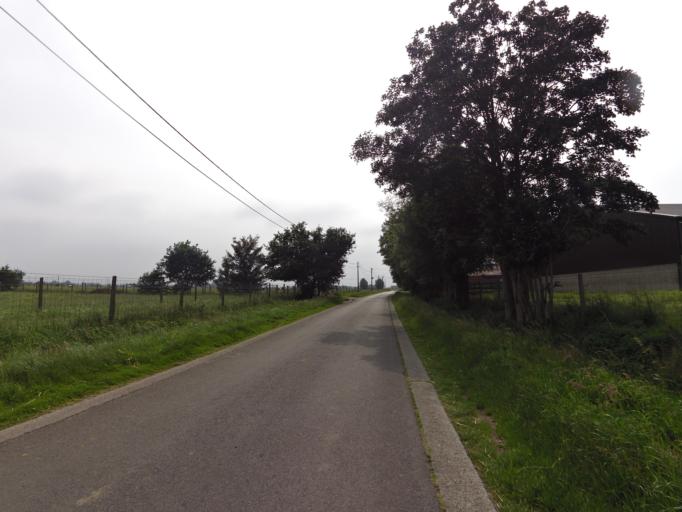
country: BE
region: Flanders
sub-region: Provincie West-Vlaanderen
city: Jabbeke
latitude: 51.1273
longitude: 3.0767
